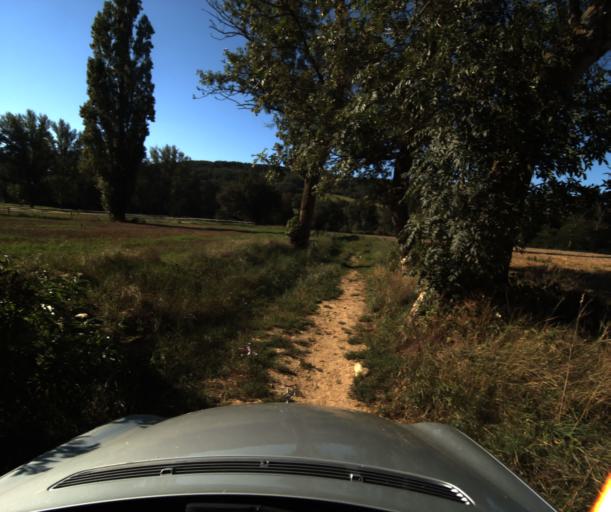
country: FR
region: Midi-Pyrenees
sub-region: Departement de l'Ariege
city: Lavelanet
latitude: 42.9907
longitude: 1.9017
